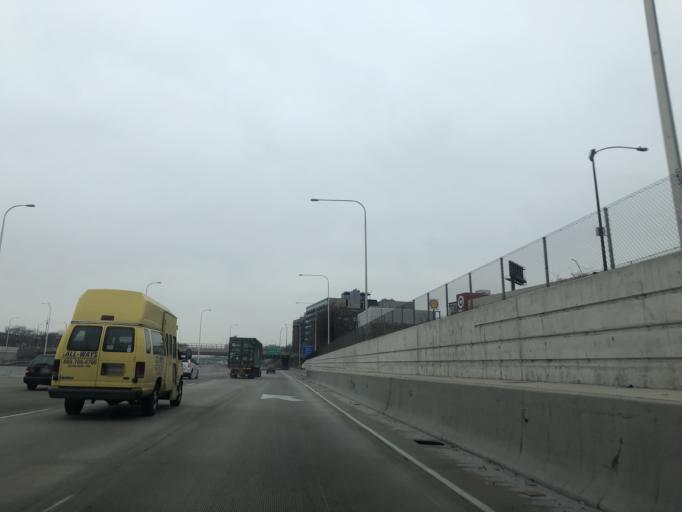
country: US
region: Illinois
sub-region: Cook County
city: Chicago
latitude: 41.8762
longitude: -87.6538
